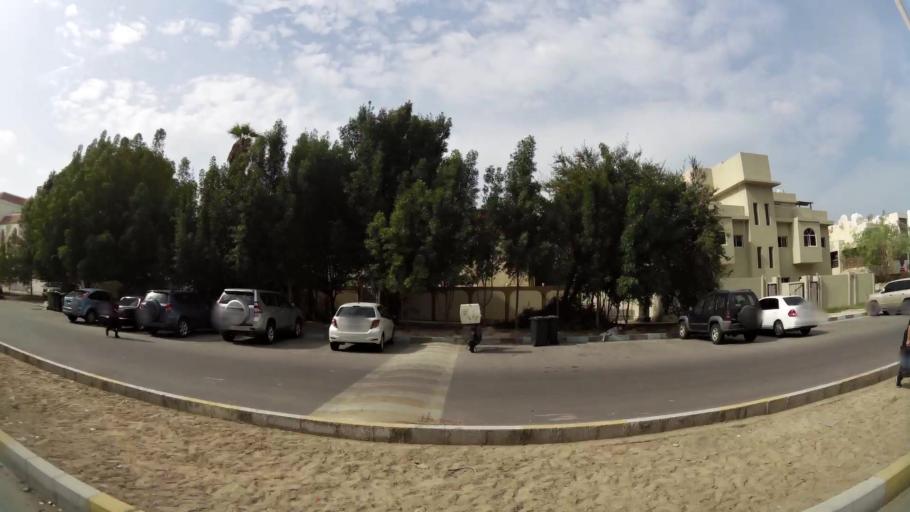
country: AE
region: Abu Dhabi
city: Abu Dhabi
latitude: 24.4528
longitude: 54.3856
